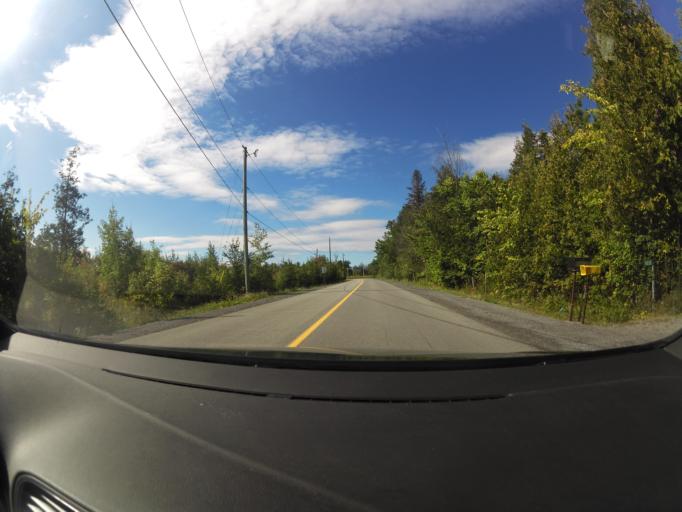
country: CA
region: Ontario
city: Bells Corners
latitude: 45.2583
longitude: -75.9686
